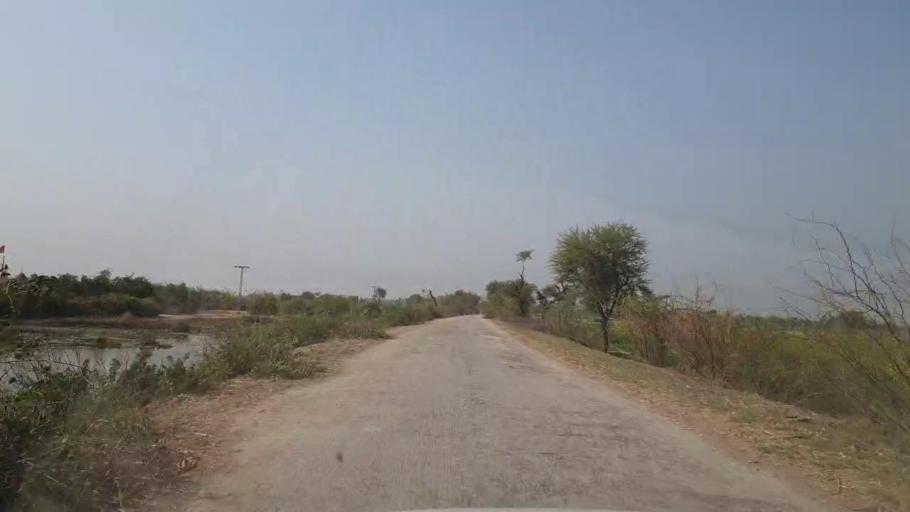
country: PK
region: Sindh
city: Mirpur Khas
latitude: 25.7012
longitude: 69.1401
